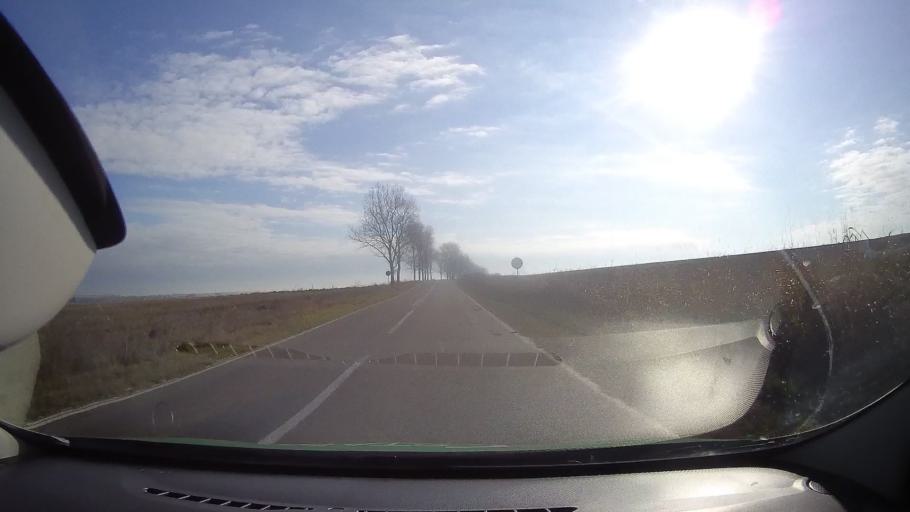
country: RO
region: Tulcea
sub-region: Comuna Mahmudia
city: Mahmudia
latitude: 45.0674
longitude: 29.1042
